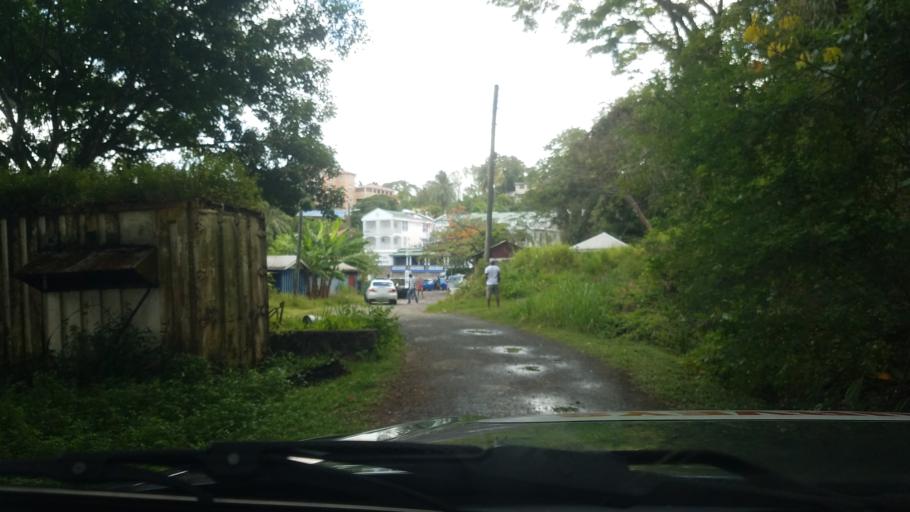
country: LC
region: Castries Quarter
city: Bisee
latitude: 14.0160
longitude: -60.9950
